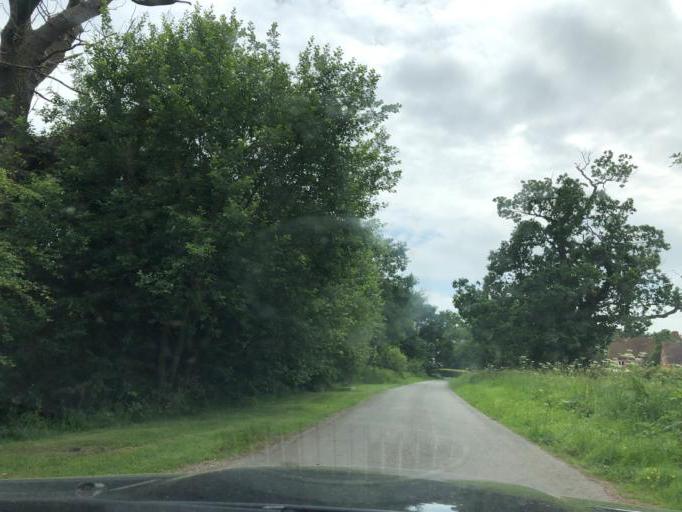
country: GB
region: England
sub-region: Warwickshire
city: Wroxall
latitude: 52.3457
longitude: -1.6434
